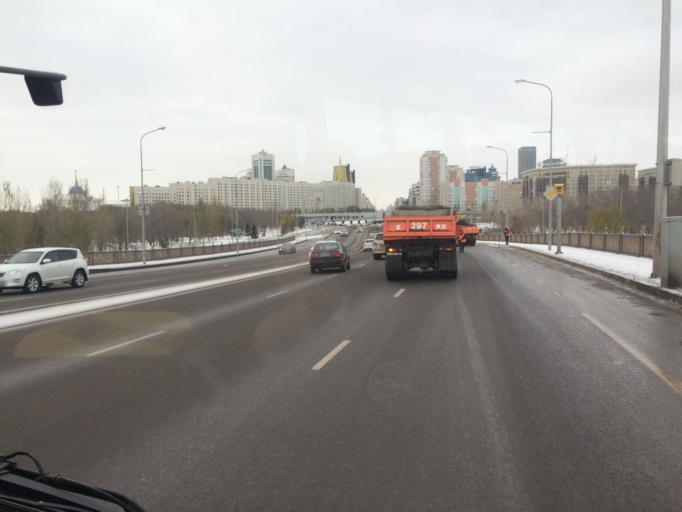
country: KZ
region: Astana Qalasy
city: Astana
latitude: 51.1364
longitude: 71.4420
